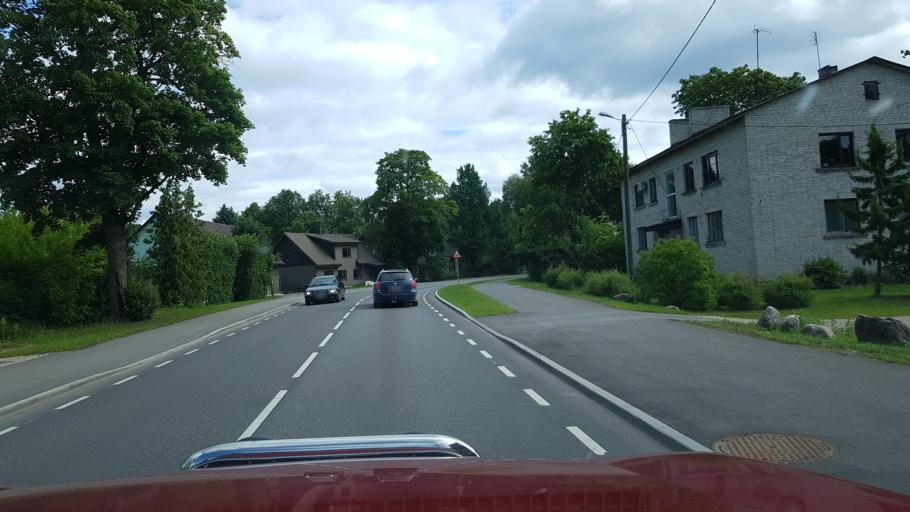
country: EE
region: Jogevamaa
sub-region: Mustvee linn
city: Mustvee
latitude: 58.8484
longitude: 26.9378
